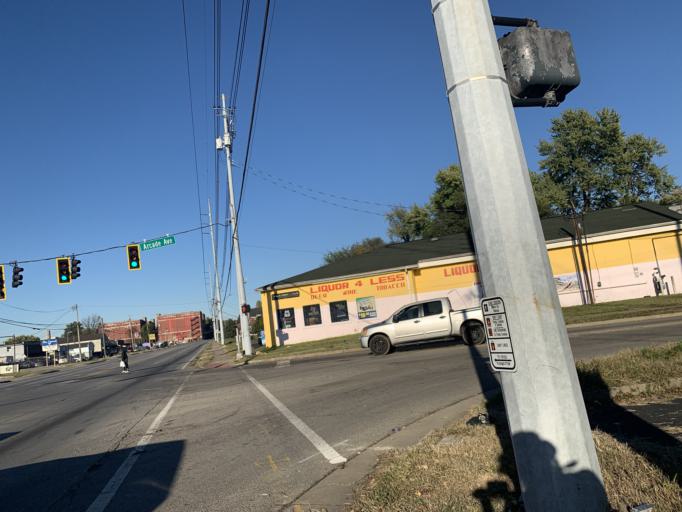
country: US
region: Kentucky
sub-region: Jefferson County
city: Shively
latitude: 38.2093
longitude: -85.7871
